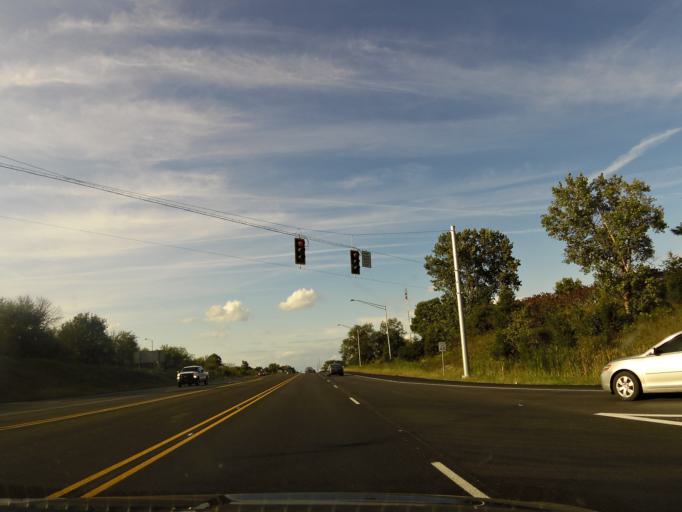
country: US
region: Indiana
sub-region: Tippecanoe County
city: Battle Ground
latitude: 40.4983
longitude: -86.8682
